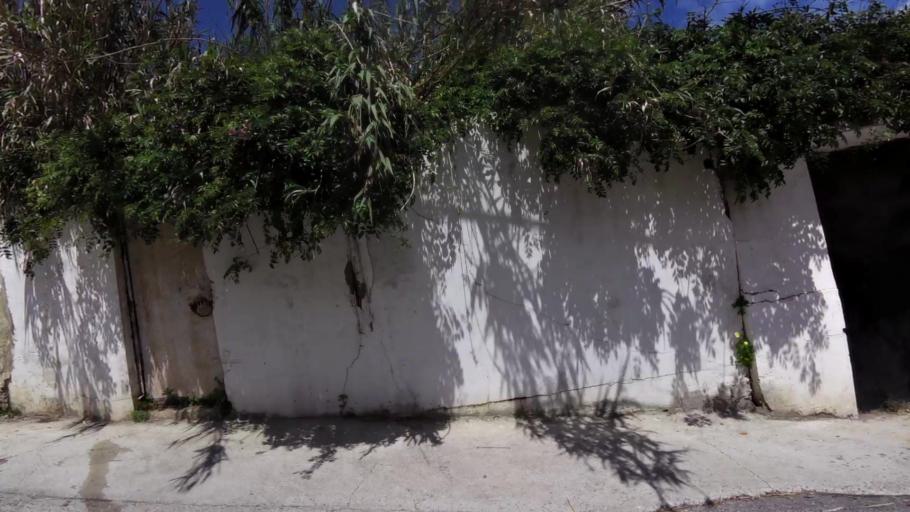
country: MA
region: Tanger-Tetouan
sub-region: Tanger-Assilah
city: Tangier
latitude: 35.7880
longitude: -5.8371
